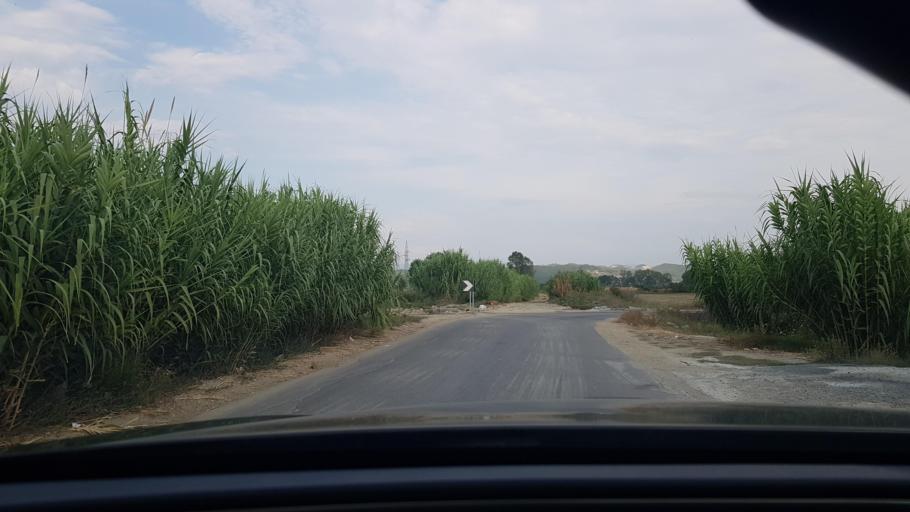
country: AL
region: Durres
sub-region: Rrethi i Durresit
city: Manze
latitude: 41.4828
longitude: 19.5362
